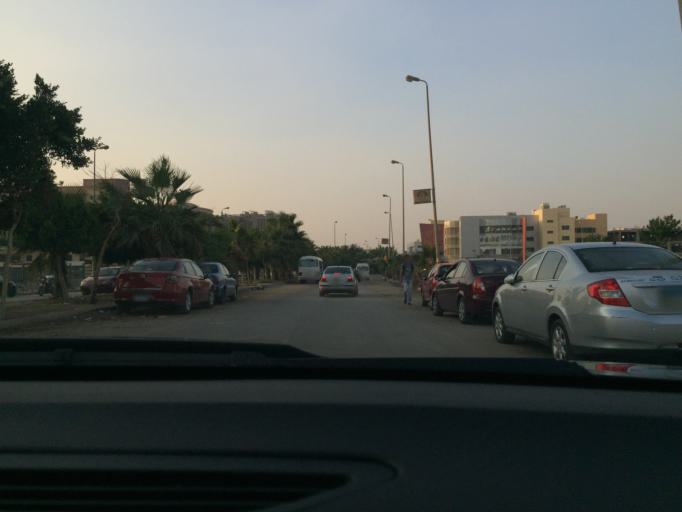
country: EG
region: Muhafazat al Qahirah
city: Cairo
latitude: 30.0169
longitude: 31.4177
